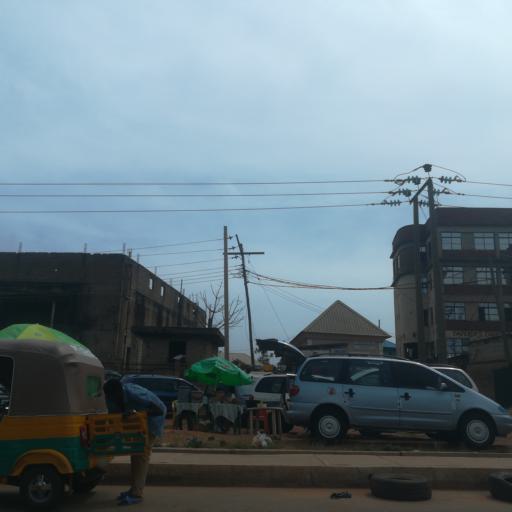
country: NG
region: Plateau
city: Jos
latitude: 9.8792
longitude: 8.8741
